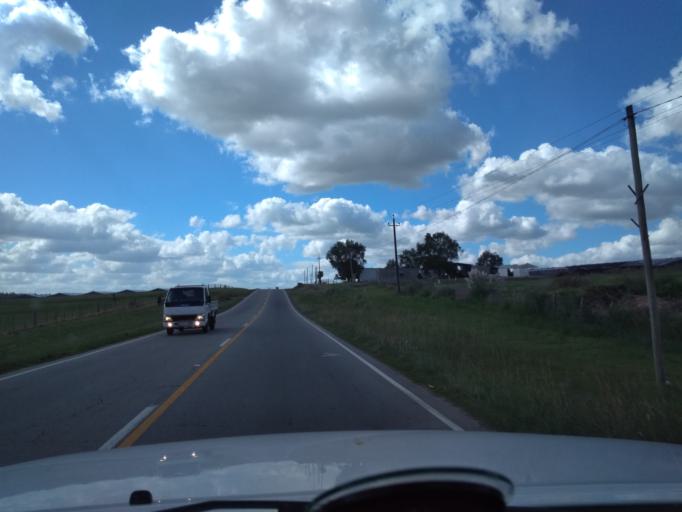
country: UY
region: Canelones
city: Joaquin Suarez
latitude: -34.7046
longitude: -56.0579
